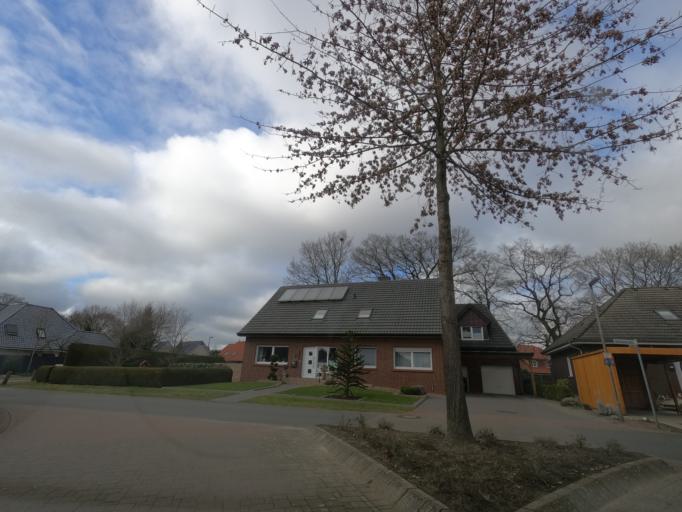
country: DE
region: Lower Saxony
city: Herzlake
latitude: 52.6893
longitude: 7.5906
